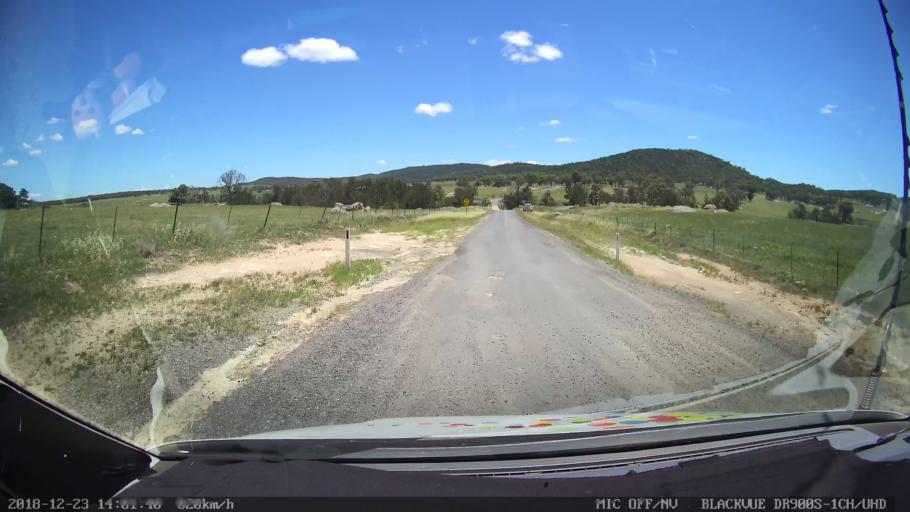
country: AU
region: New South Wales
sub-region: Tamworth Municipality
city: Manilla
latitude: -30.6216
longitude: 151.1109
